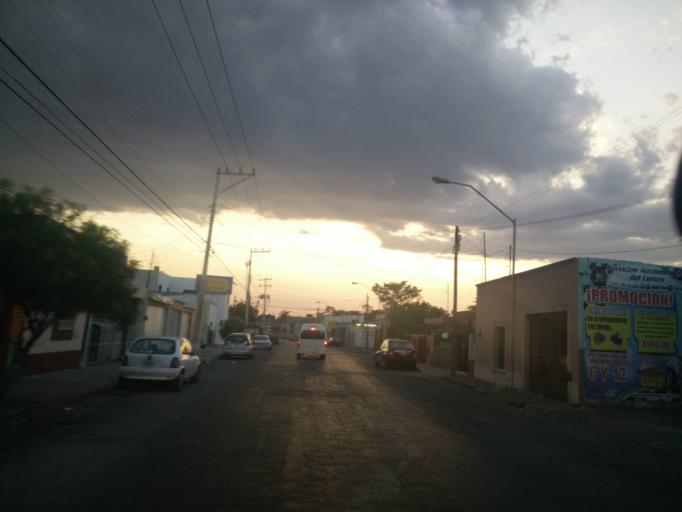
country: MX
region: Yucatan
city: Merida
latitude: 20.9638
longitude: -89.6378
